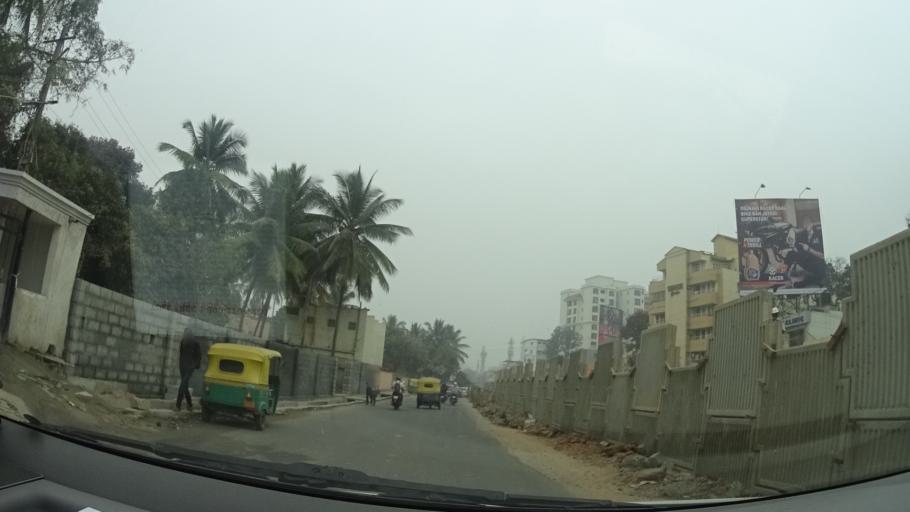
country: IN
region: Karnataka
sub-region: Bangalore Urban
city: Bangalore
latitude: 13.0290
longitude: 77.6336
